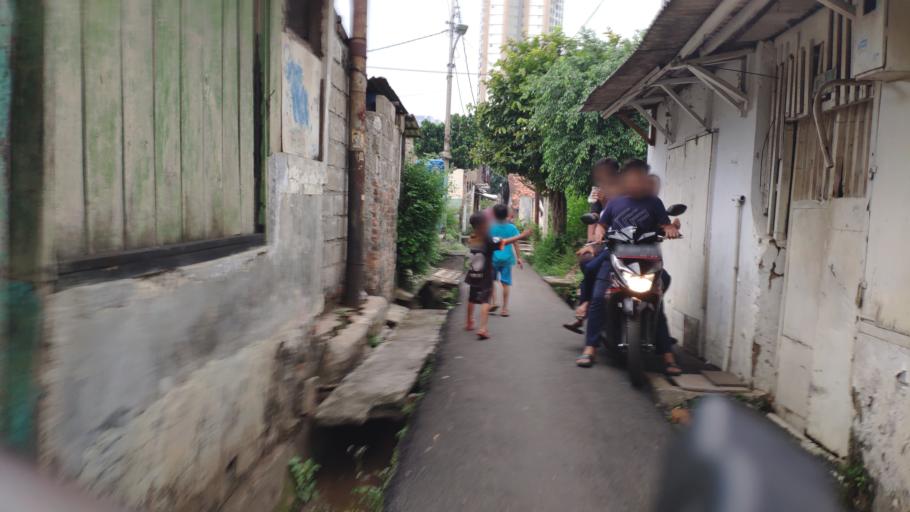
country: ID
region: Jakarta Raya
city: Jakarta
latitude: -6.2118
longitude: 106.8370
